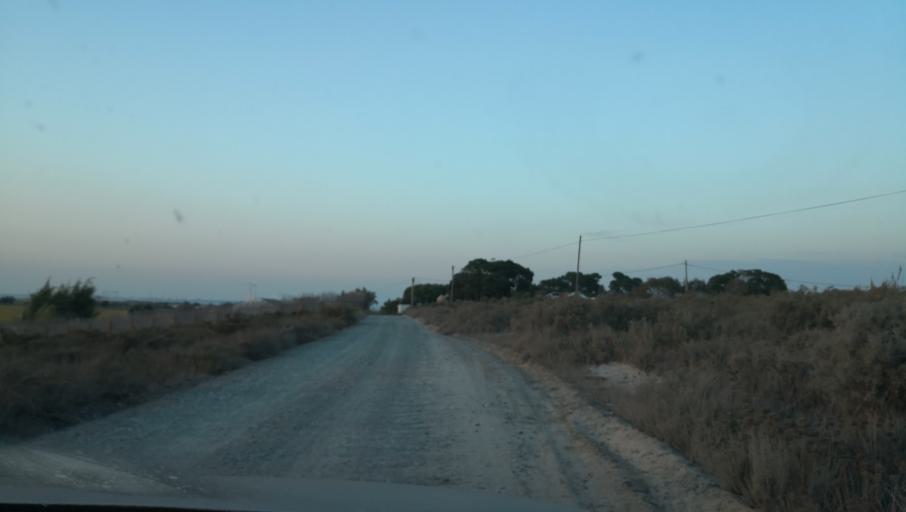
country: PT
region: Setubal
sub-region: Setubal
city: Setubal
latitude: 38.4026
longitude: -8.7737
